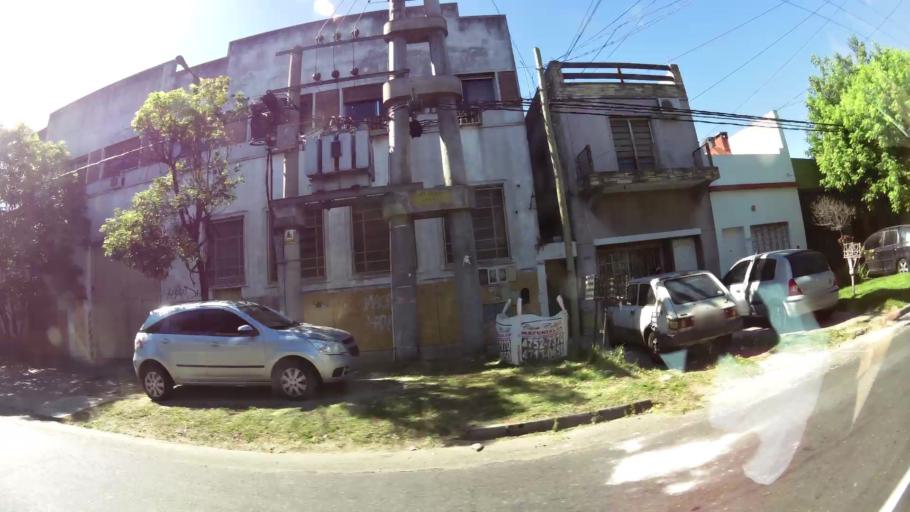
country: AR
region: Buenos Aires
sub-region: Partido de General San Martin
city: General San Martin
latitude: -34.5385
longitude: -58.5211
